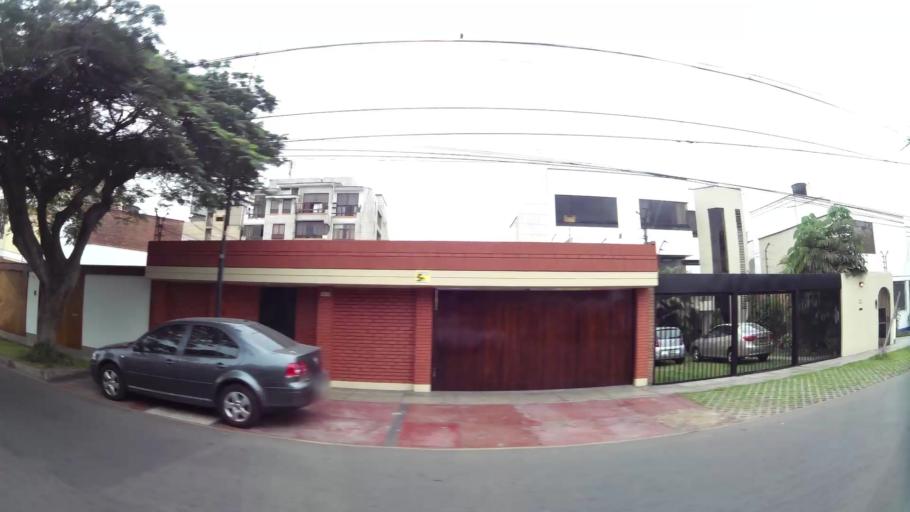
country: PE
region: Lima
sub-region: Lima
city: San Luis
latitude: -12.0927
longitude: -77.0145
